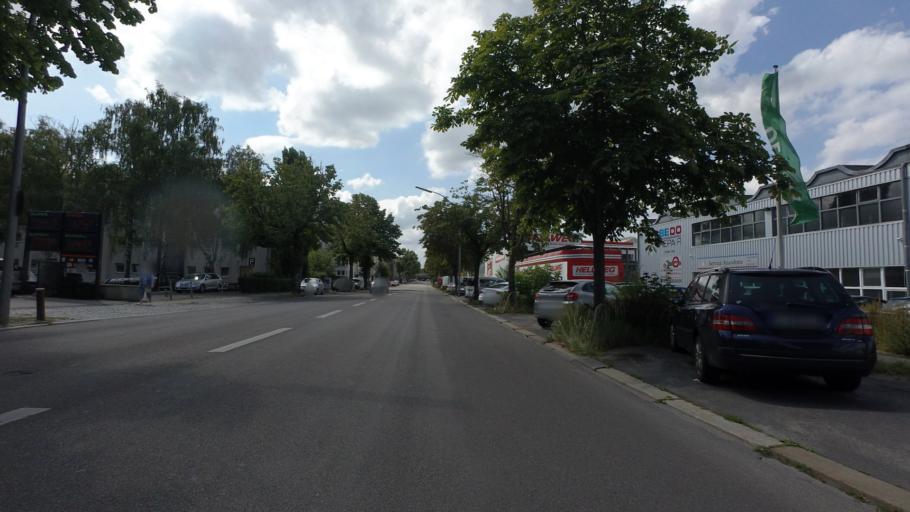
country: DE
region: Berlin
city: Mariendorf
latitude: 52.4493
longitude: 13.3660
